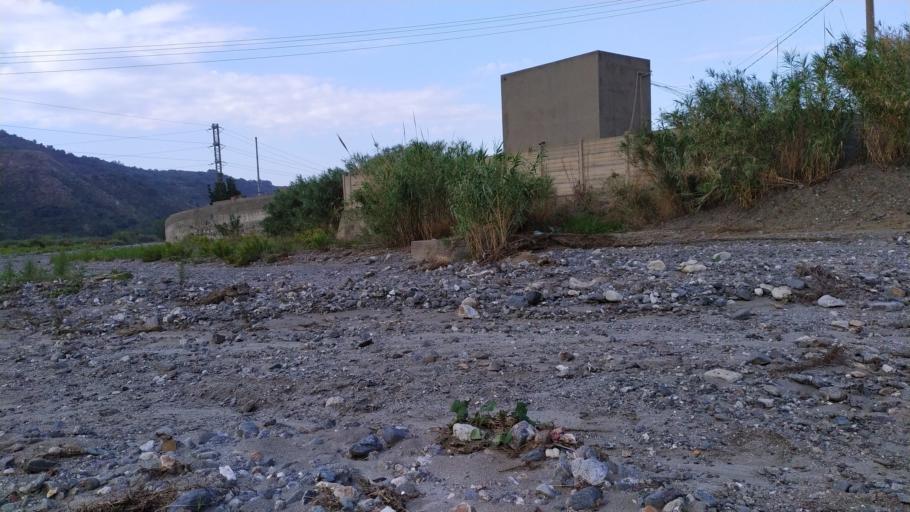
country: IT
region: Sicily
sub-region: Messina
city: Saponara
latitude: 38.2031
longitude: 15.4302
